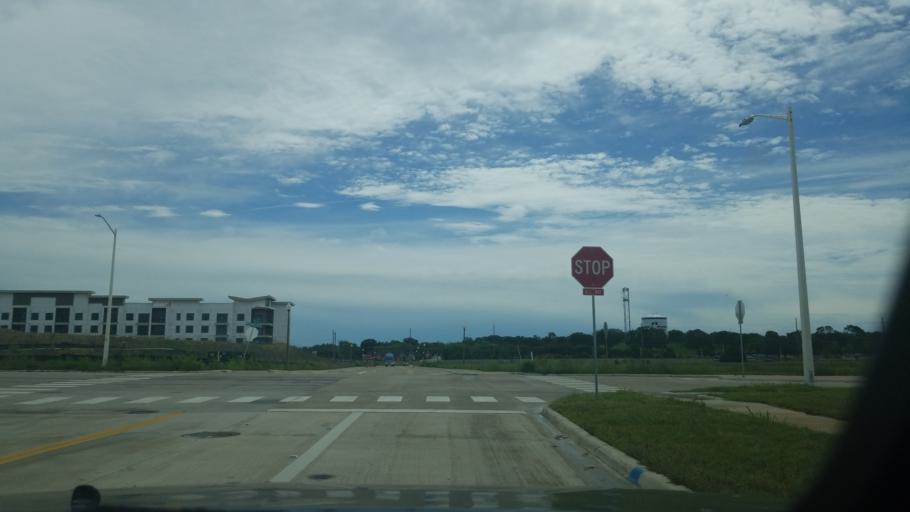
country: US
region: Texas
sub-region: Denton County
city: Denton
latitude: 33.2216
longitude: -97.1665
